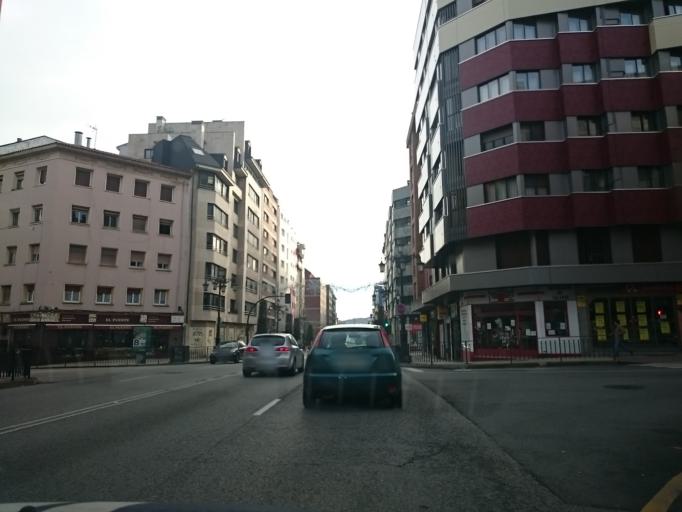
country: ES
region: Asturias
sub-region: Province of Asturias
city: Oviedo
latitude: 43.3600
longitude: -5.8387
